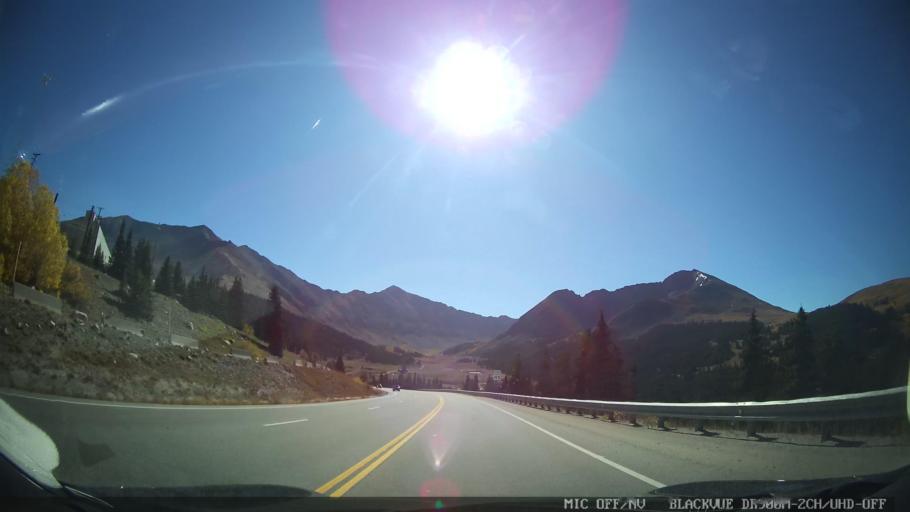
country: US
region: Colorado
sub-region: Lake County
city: Leadville
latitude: 39.3669
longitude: -106.1873
